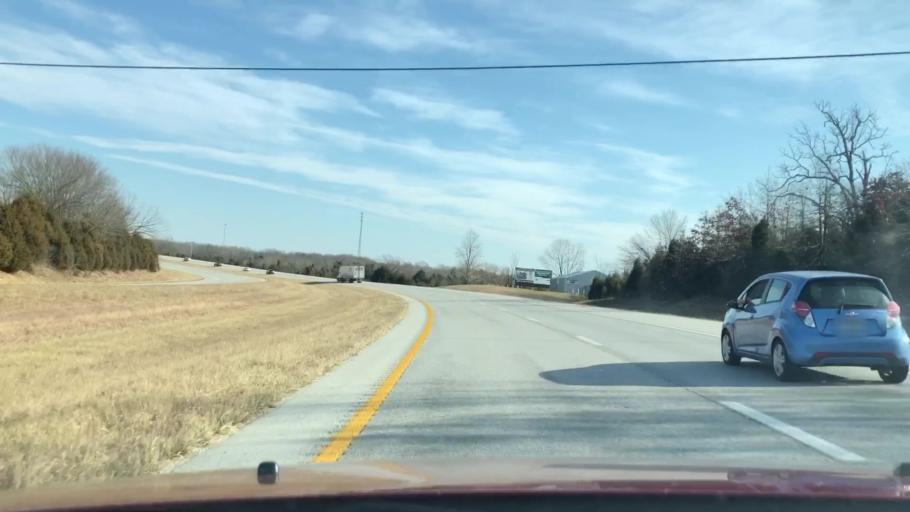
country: US
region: Missouri
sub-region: Webster County
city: Rogersville
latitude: 37.1522
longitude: -92.9398
